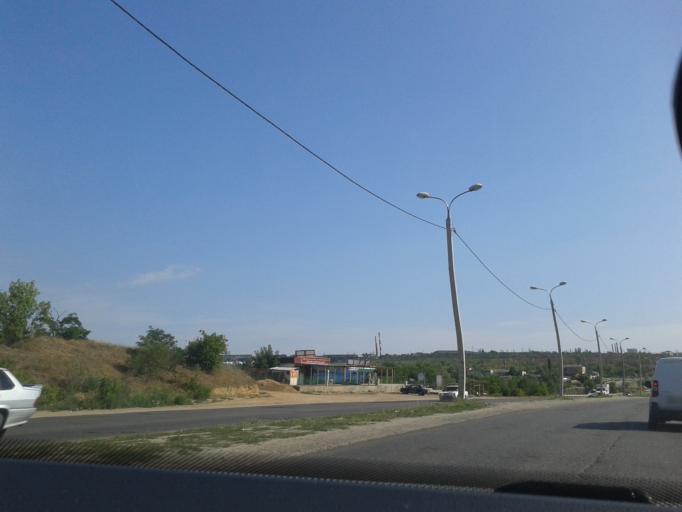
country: RU
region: Volgograd
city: Volgograd
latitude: 48.7285
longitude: 44.4494
